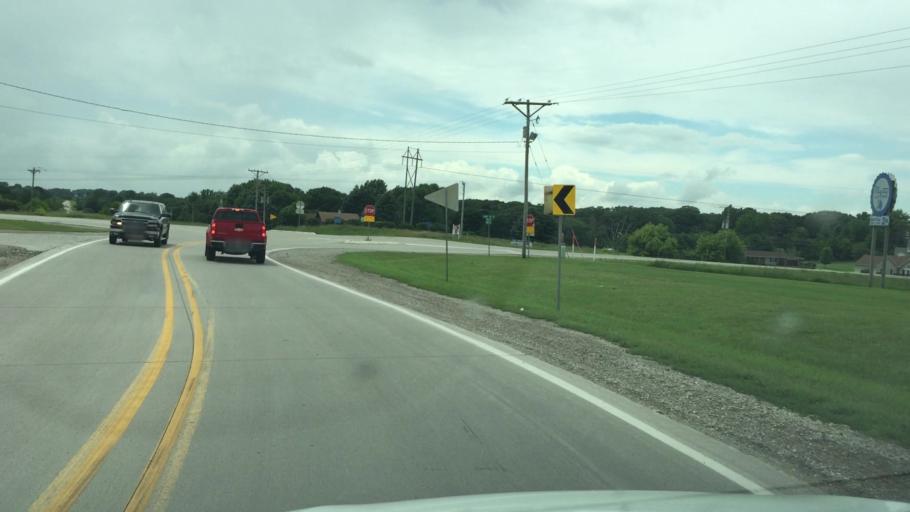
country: US
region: Iowa
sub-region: Jasper County
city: Newton
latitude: 41.7208
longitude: -93.0587
